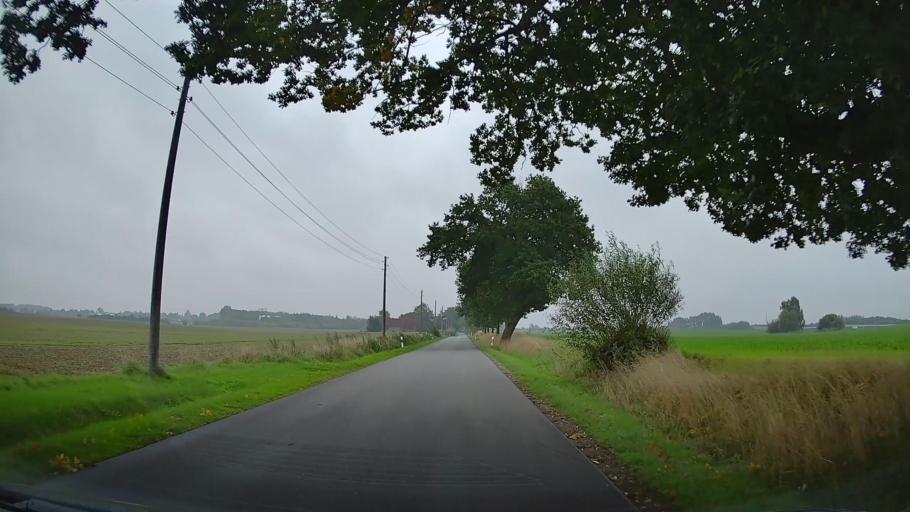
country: DE
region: Mecklenburg-Vorpommern
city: Hornstorf
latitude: 53.9043
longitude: 11.5138
